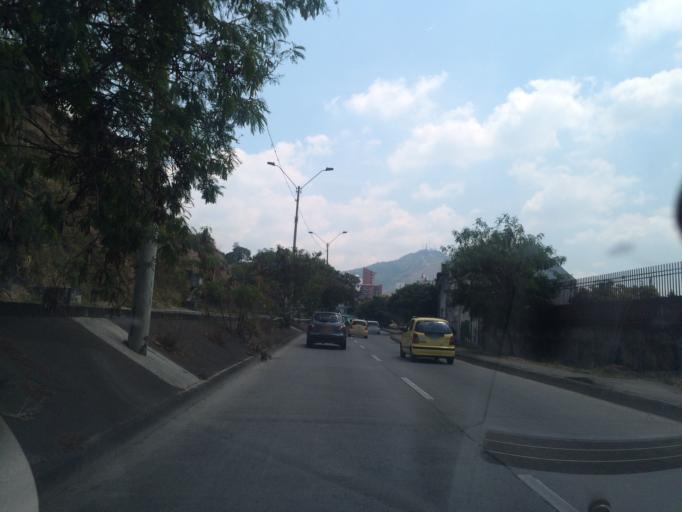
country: CO
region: Valle del Cauca
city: Cali
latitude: 3.4389
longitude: -76.5489
